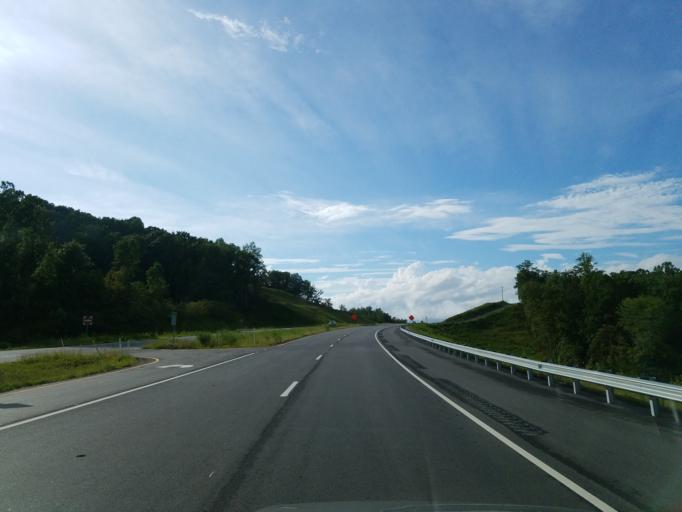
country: US
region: Georgia
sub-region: White County
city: Cleveland
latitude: 34.5843
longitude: -83.7747
